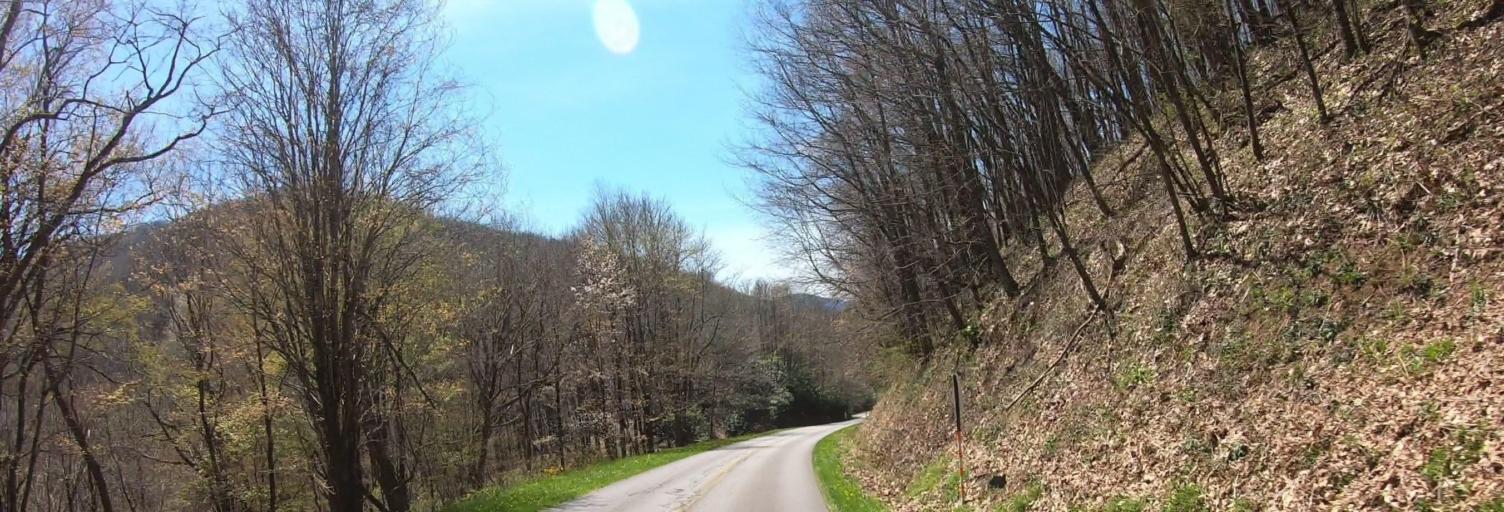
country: US
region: North Carolina
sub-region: Haywood County
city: Maggie Valley
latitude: 35.5003
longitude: -83.1553
